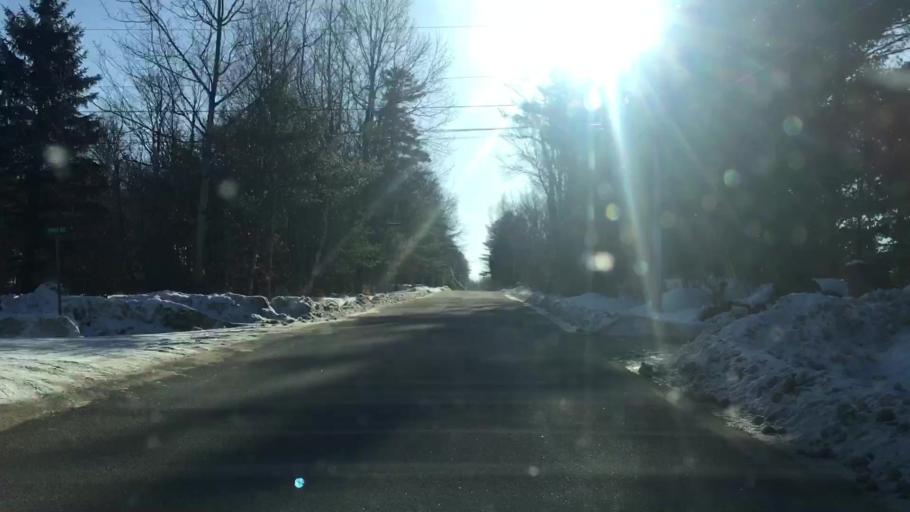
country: US
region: Maine
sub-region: Oxford County
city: Paris
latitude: 44.2748
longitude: -70.5067
